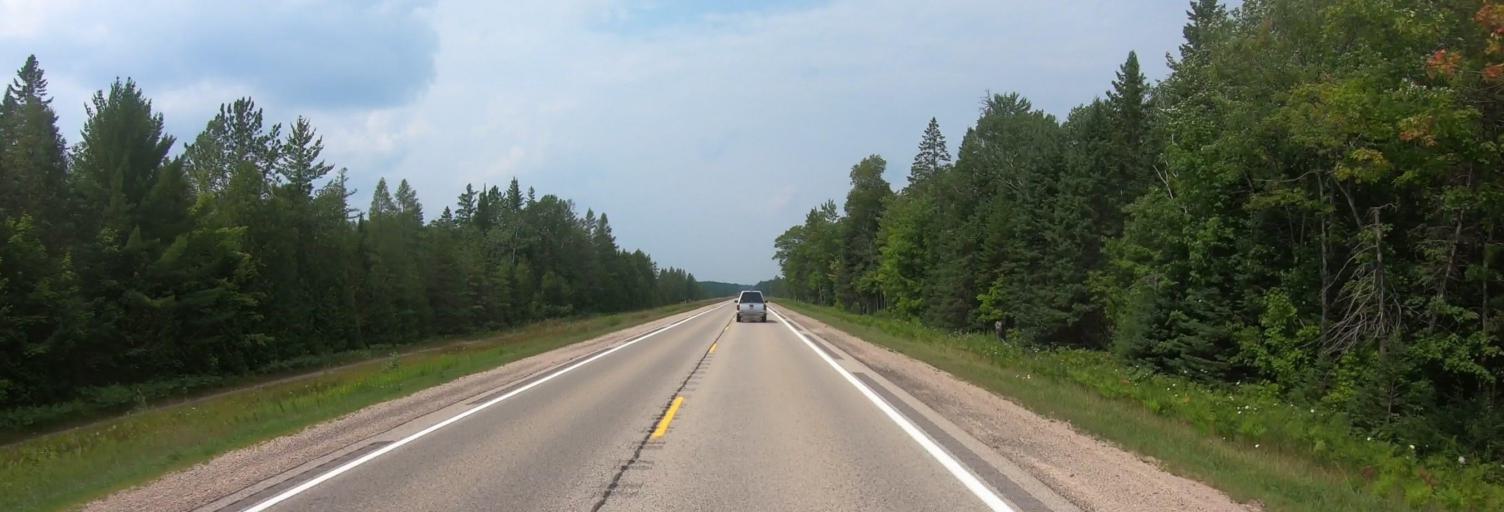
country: US
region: Michigan
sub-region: Alger County
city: Munising
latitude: 46.3761
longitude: -86.5602
